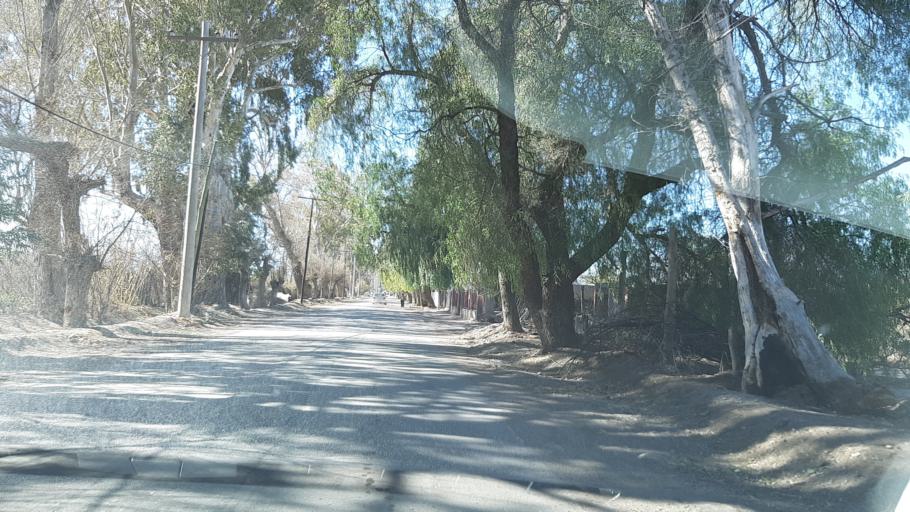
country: AR
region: San Juan
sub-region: Departamento de Zonda
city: Zonda
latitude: -31.4696
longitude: -68.7497
